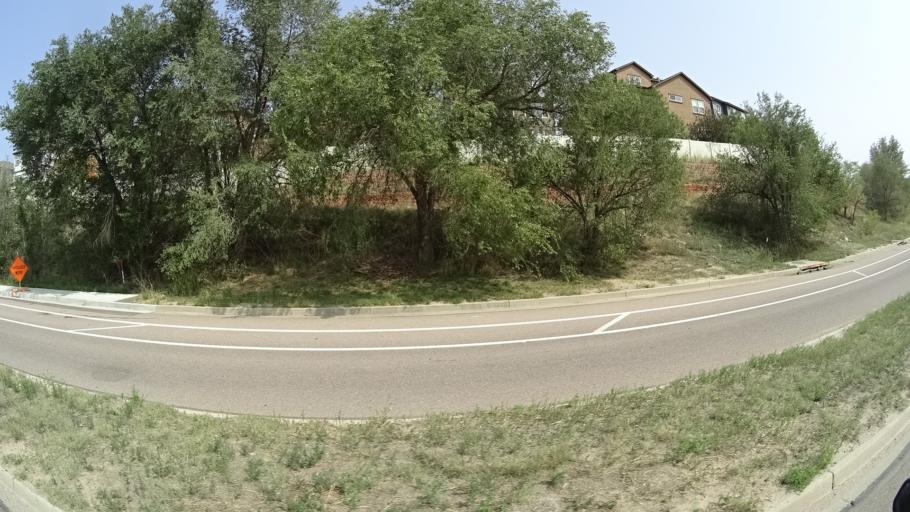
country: US
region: Colorado
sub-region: El Paso County
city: Stratmoor
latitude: 38.8070
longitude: -104.7906
